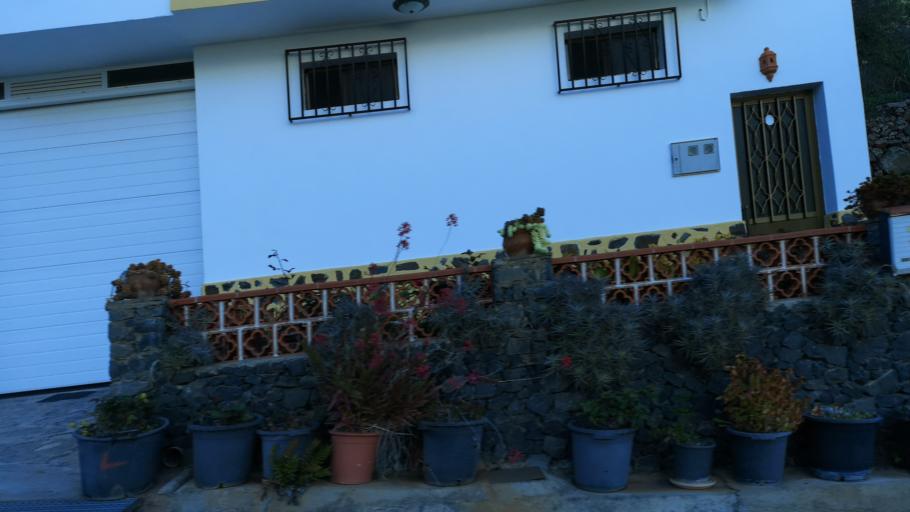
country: ES
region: Canary Islands
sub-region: Provincia de Santa Cruz de Tenerife
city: Alajero
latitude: 28.0648
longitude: -17.2375
